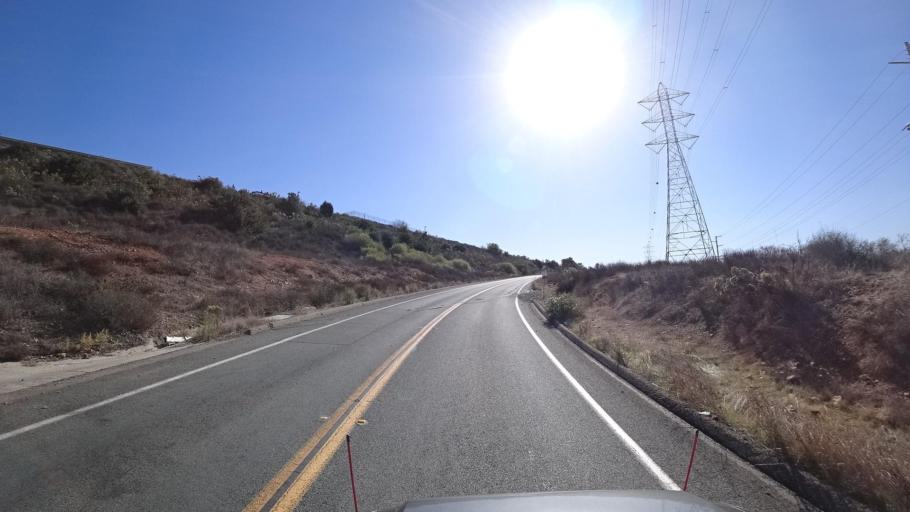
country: MX
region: Baja California
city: Tijuana
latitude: 32.5914
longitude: -116.9253
